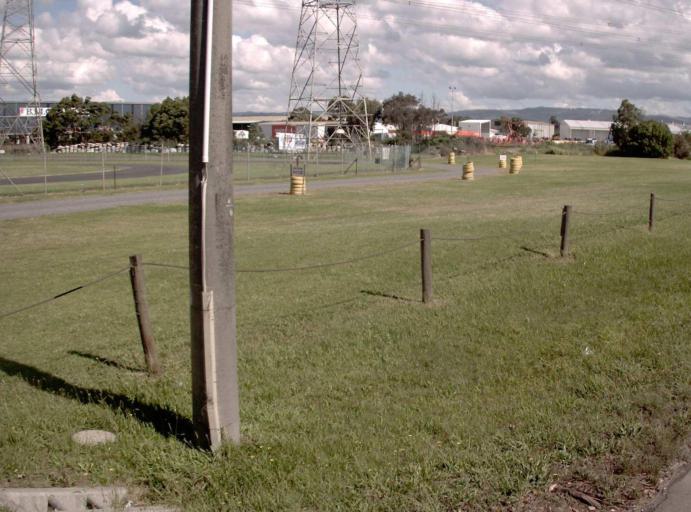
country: AU
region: Victoria
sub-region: Latrobe
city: Morwell
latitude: -38.2346
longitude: 146.4385
